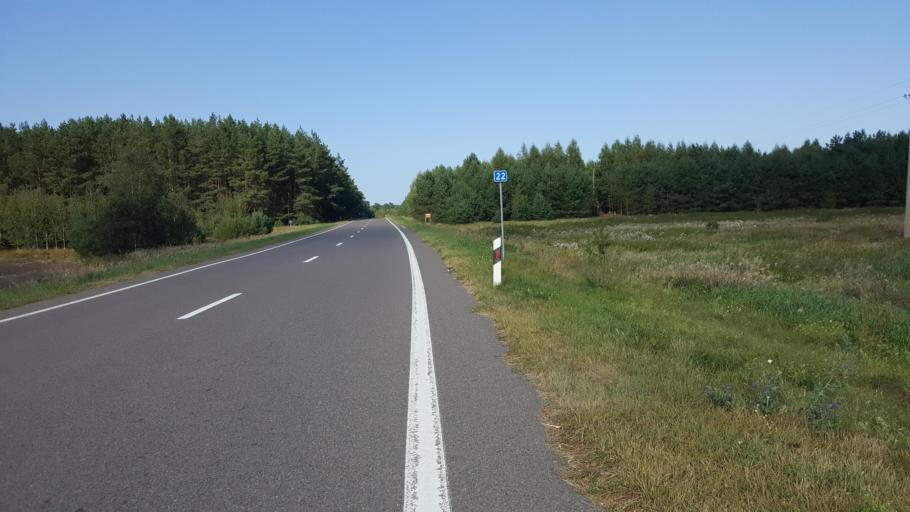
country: PL
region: Podlasie
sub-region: Powiat hajnowski
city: Hajnowka
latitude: 52.5594
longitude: 23.6043
